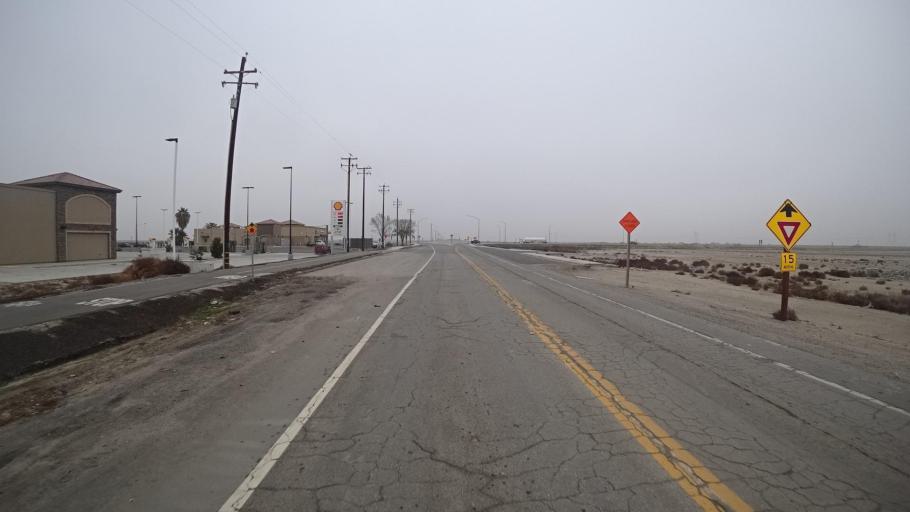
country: US
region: California
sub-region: Kern County
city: Rosedale
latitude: 35.2658
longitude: -119.2527
